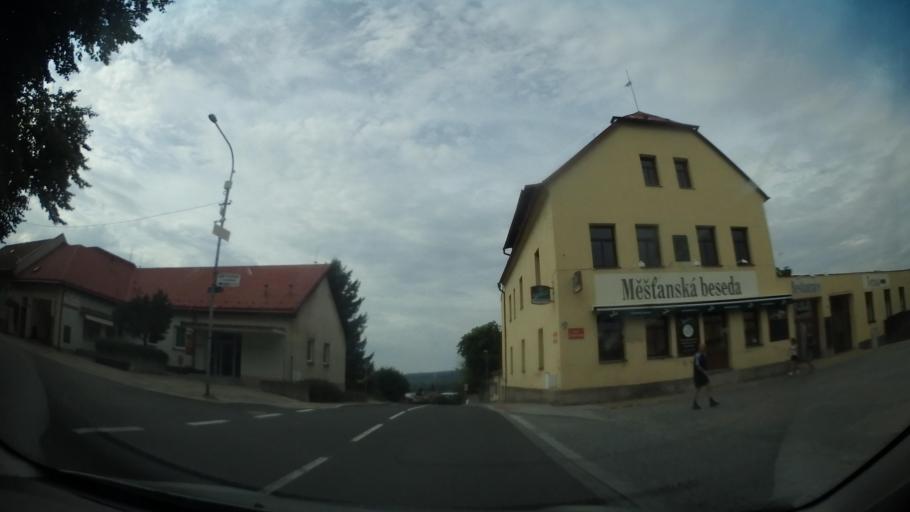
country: CZ
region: Pardubicky
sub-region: Okres Chrudim
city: Sec
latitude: 49.8474
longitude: 15.6575
